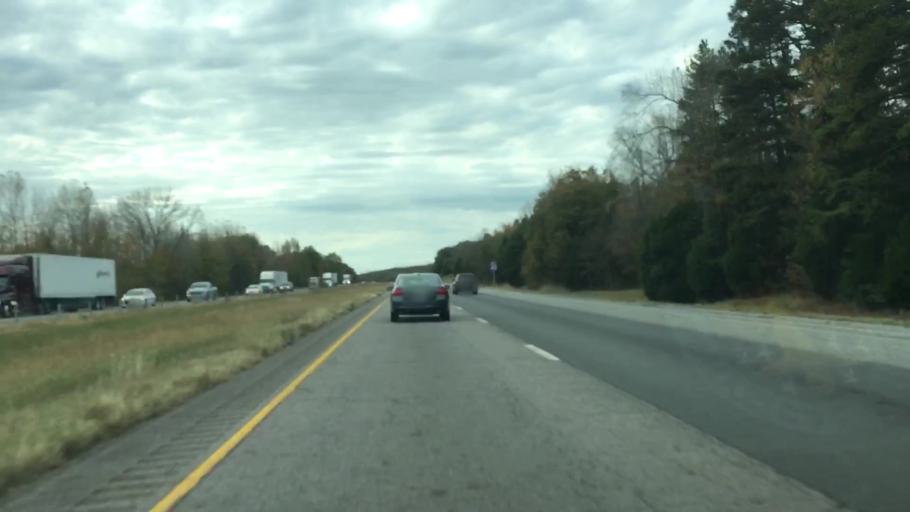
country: US
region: Arkansas
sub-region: Faulkner County
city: Conway
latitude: 35.1549
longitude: -92.5591
